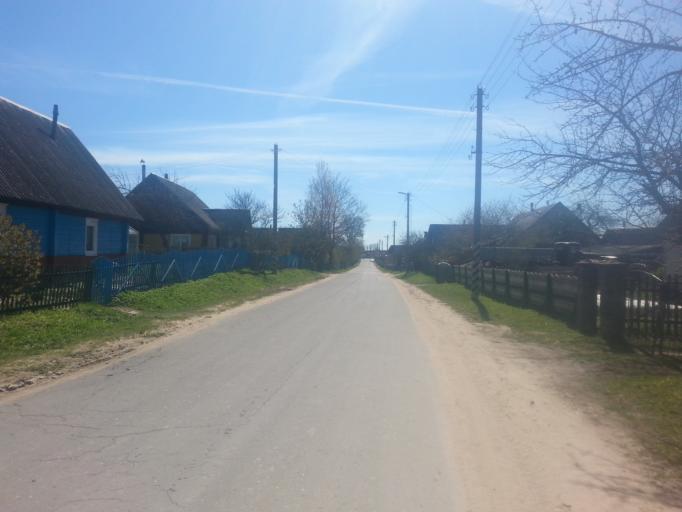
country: BY
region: Minsk
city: Narach
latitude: 54.9403
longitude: 26.6917
